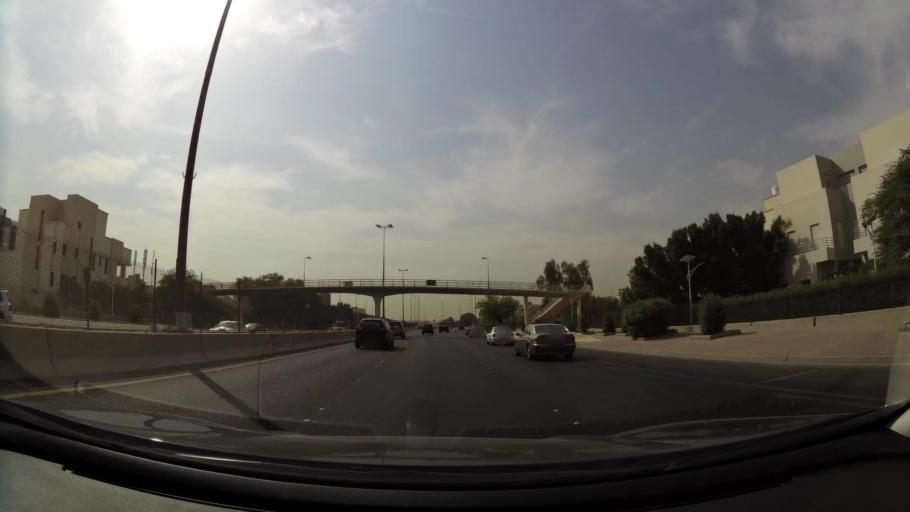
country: KW
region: Al Asimah
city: Ash Shamiyah
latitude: 29.3367
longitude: 47.9716
